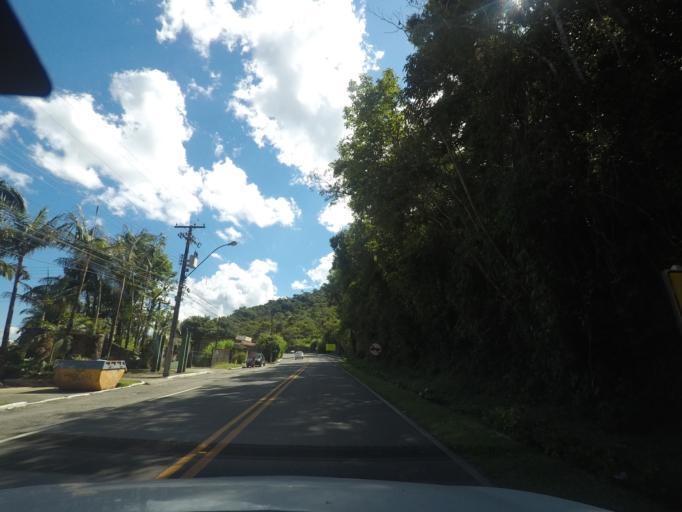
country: BR
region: Rio de Janeiro
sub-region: Teresopolis
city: Teresopolis
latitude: -22.4586
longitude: -42.9867
